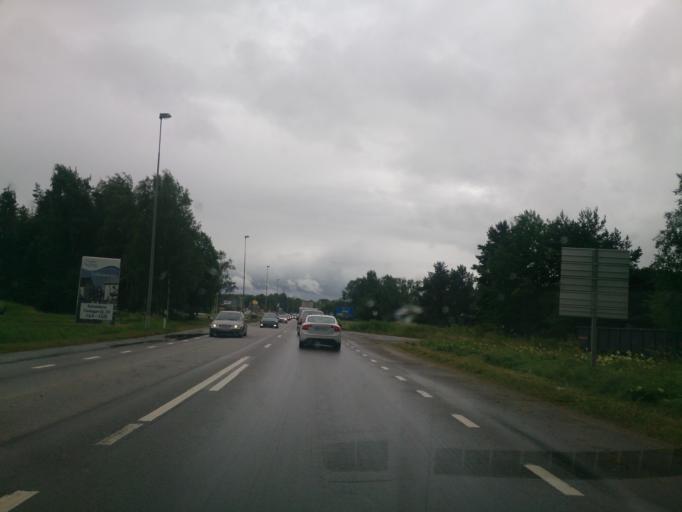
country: SE
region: OEstergoetland
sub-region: Soderkopings Kommun
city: Soederkoeping
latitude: 58.4876
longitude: 16.3099
